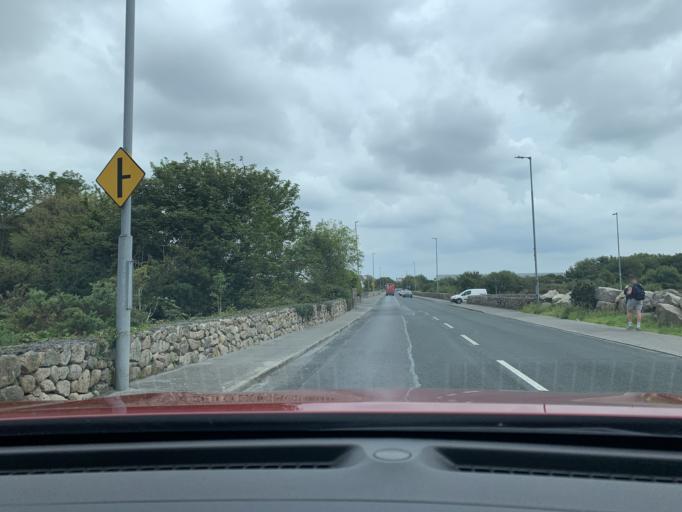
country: IE
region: Connaught
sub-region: County Galway
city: Gaillimh
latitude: 53.2774
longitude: -9.0979
